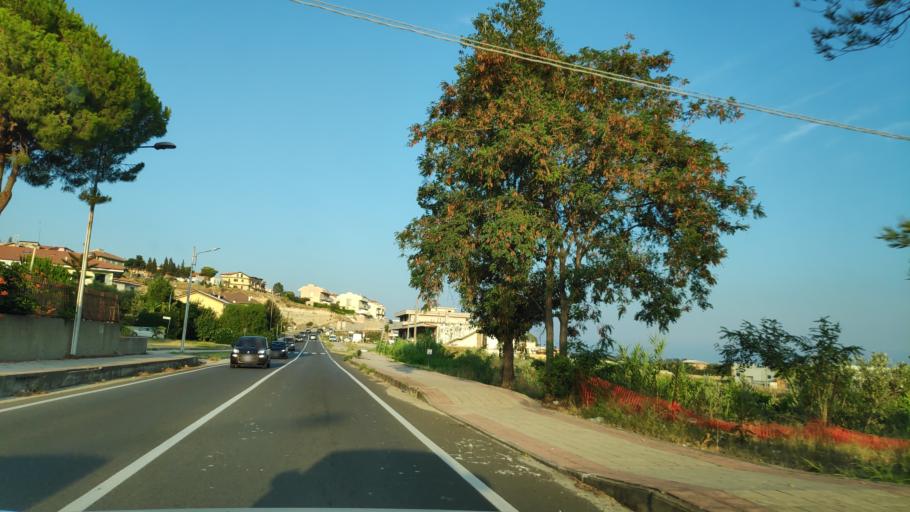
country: IT
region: Calabria
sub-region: Provincia di Catanzaro
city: Martelli-Laganosa
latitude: 38.6792
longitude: 16.5333
